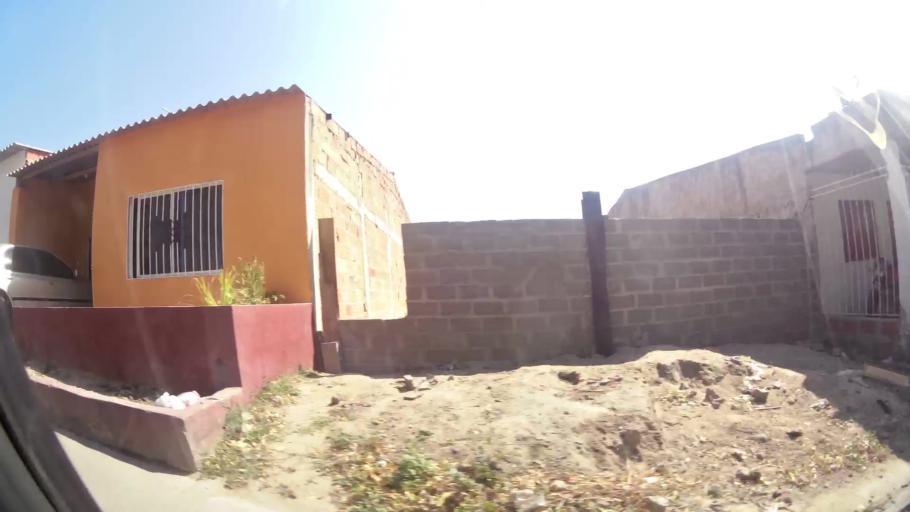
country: CO
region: Atlantico
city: Barranquilla
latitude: 10.9808
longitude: -74.8293
